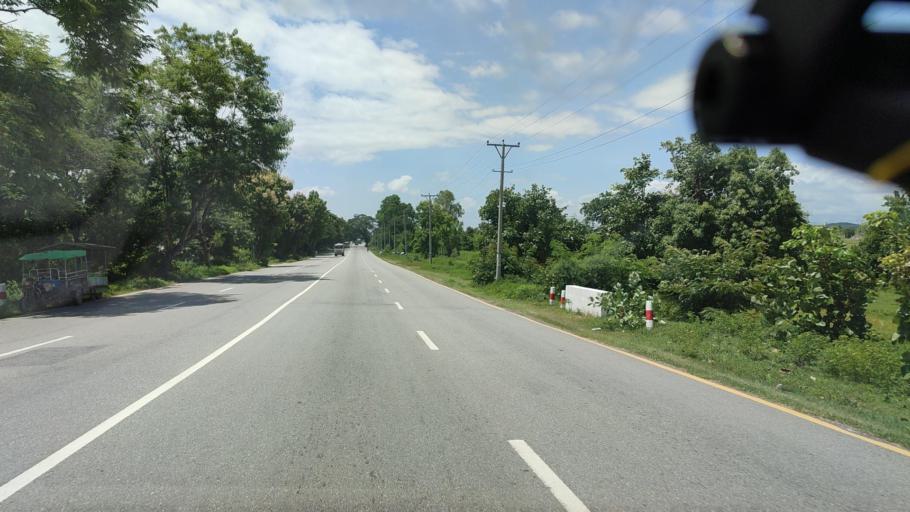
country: MM
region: Mandalay
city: Pyinmana
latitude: 20.0297
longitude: 96.2463
